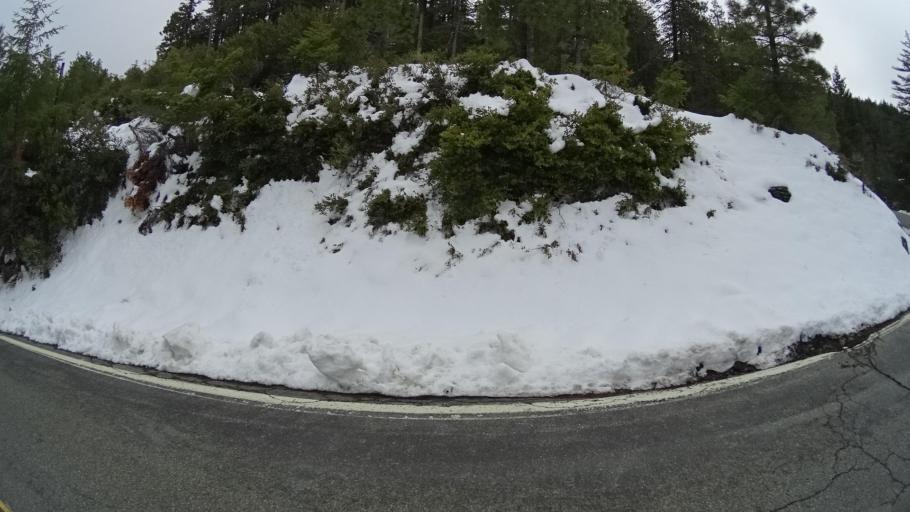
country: US
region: California
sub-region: Humboldt County
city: Willow Creek
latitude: 40.8648
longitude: -123.7382
